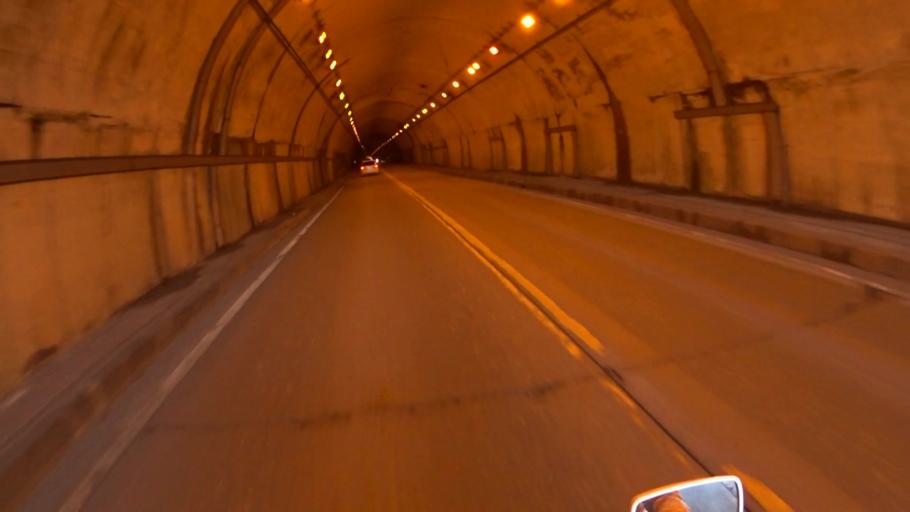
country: JP
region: Kyoto
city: Miyazu
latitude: 35.4485
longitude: 135.0736
